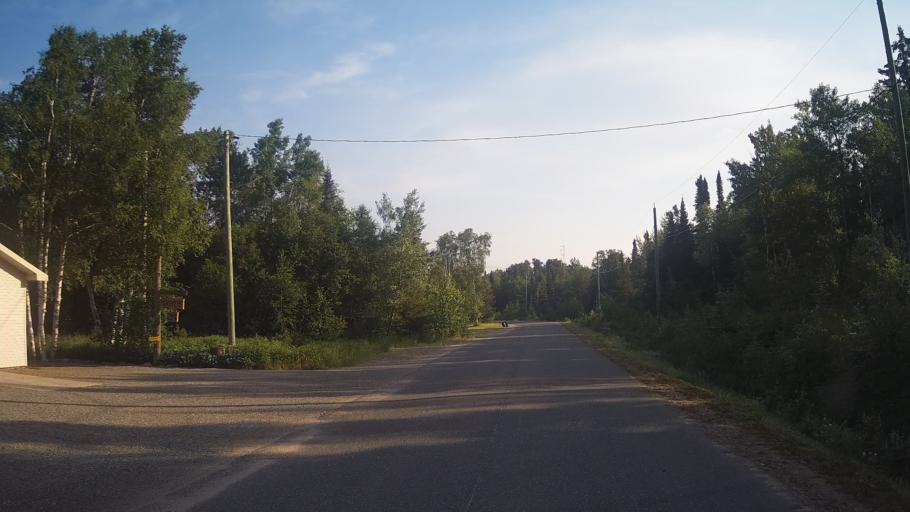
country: CA
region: Ontario
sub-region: Rainy River District
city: Atikokan
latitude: 49.4003
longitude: -91.6658
